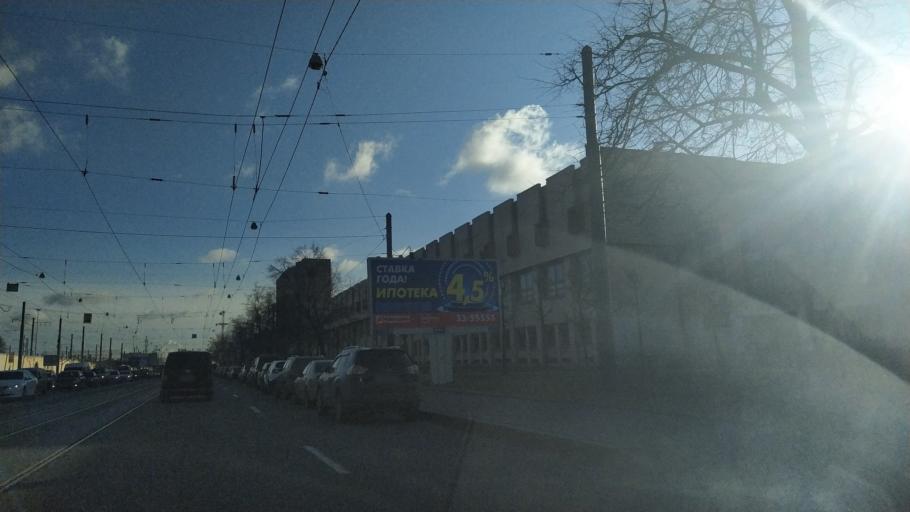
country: RU
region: Leningrad
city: Sampsonievskiy
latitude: 59.9768
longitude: 30.3443
